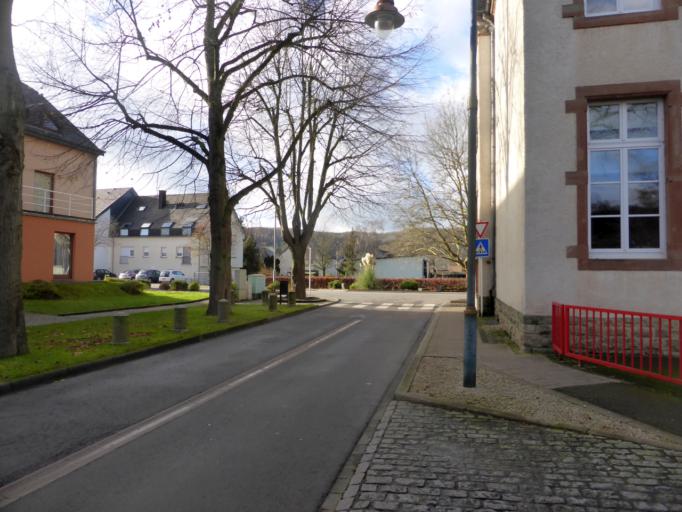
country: LU
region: Diekirch
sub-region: Canton de Diekirch
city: Erpeldange
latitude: 49.8635
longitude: 6.1135
